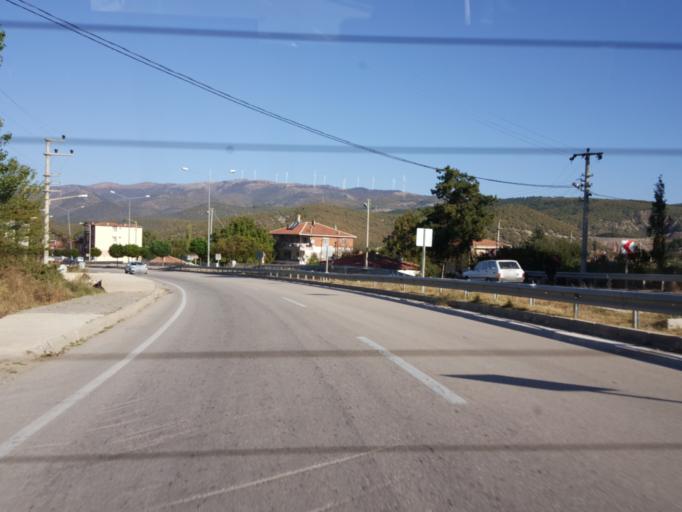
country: TR
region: Amasya
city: Ezinepazari
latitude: 40.5681
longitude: 36.1397
